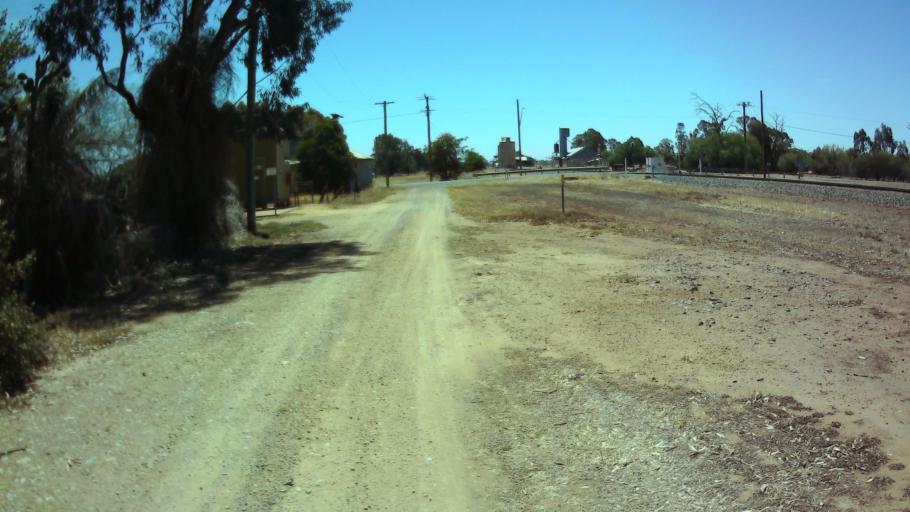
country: AU
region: New South Wales
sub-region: Weddin
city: Grenfell
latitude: -33.8449
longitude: 147.7410
